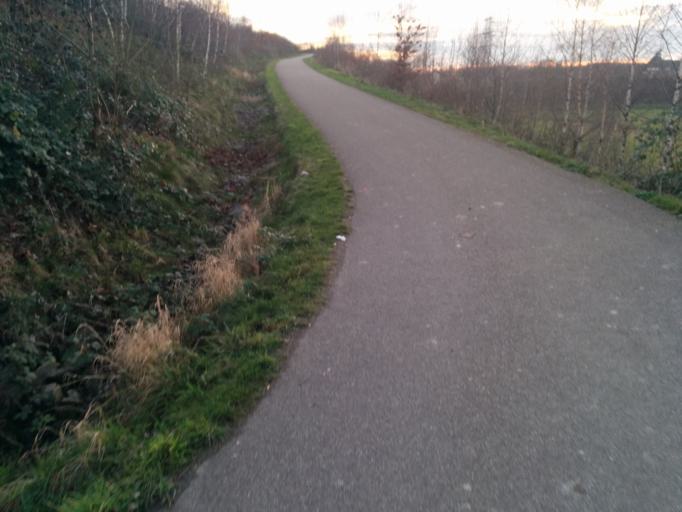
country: DE
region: North Rhine-Westphalia
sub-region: Regierungsbezirk Dusseldorf
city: Hochfeld
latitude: 51.3764
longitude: 6.7373
